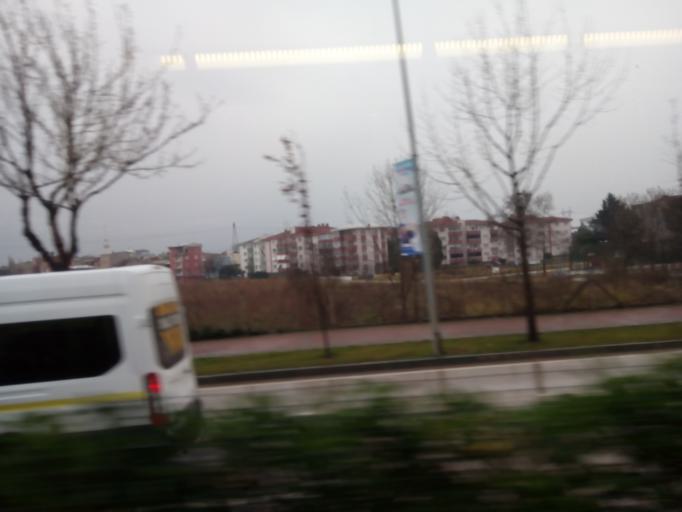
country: TR
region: Bursa
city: Yildirim
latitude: 40.2076
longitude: 29.0276
